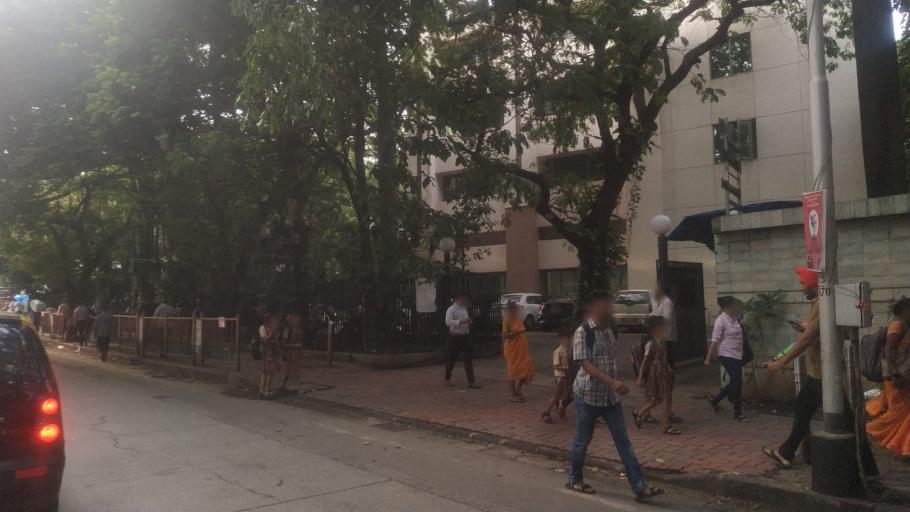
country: IN
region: Maharashtra
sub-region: Mumbai Suburban
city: Mumbai
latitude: 19.0413
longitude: 72.8652
